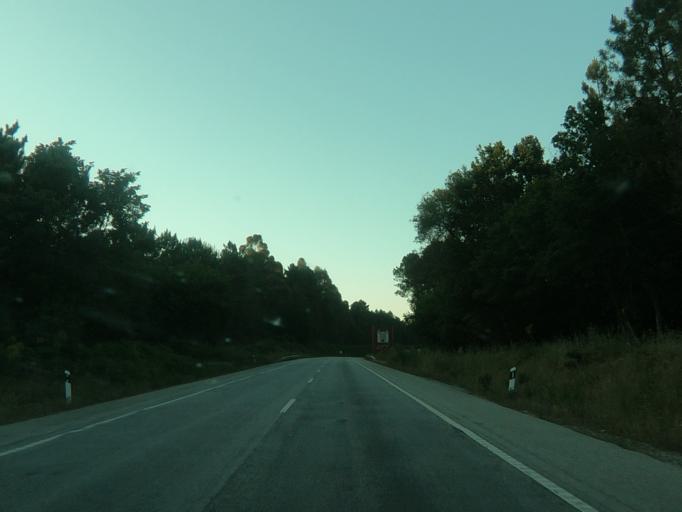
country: PT
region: Viseu
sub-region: Viseu
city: Rio de Loba
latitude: 40.6643
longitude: -7.8621
